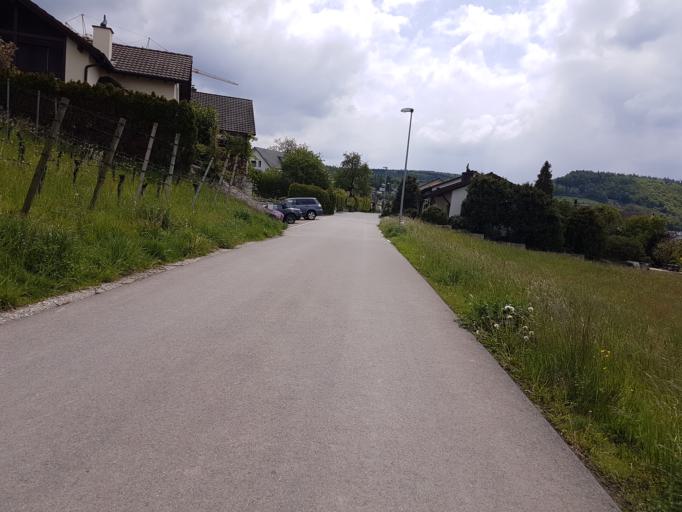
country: CH
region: Aargau
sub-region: Bezirk Baden
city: Wurenlingen
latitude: 47.5402
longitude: 8.2565
